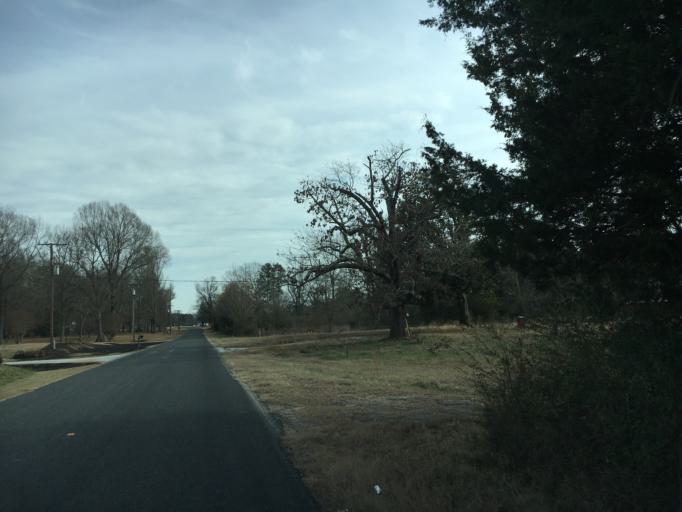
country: US
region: South Carolina
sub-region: Laurens County
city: Laurens
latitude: 34.3634
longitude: -81.9745
